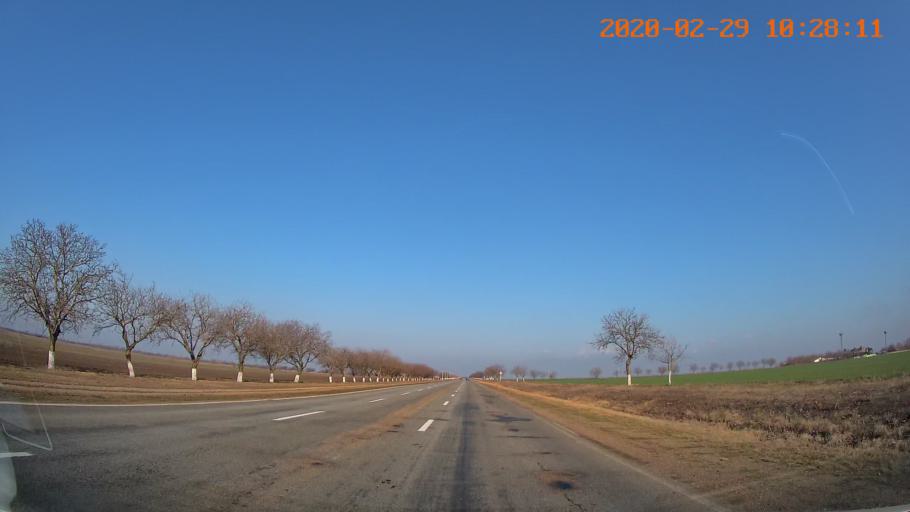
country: MD
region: Telenesti
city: Tiraspolul Nou
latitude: 46.9068
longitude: 29.5930
